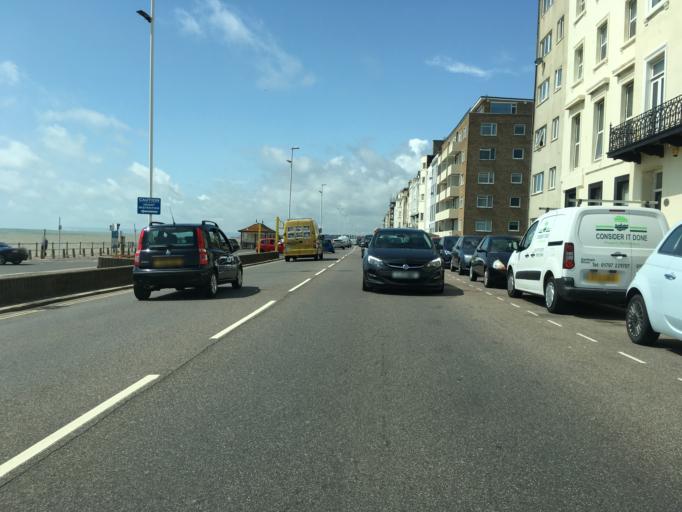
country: GB
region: England
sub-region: East Sussex
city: Saint Leonards-on-Sea
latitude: 50.8508
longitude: 0.5521
